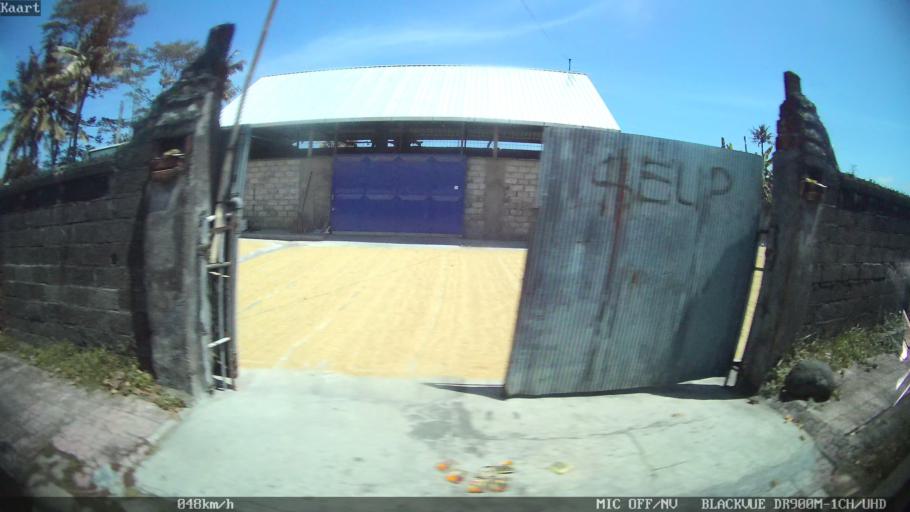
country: ID
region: Bali
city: Klungkung
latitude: -8.5664
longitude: 115.3444
